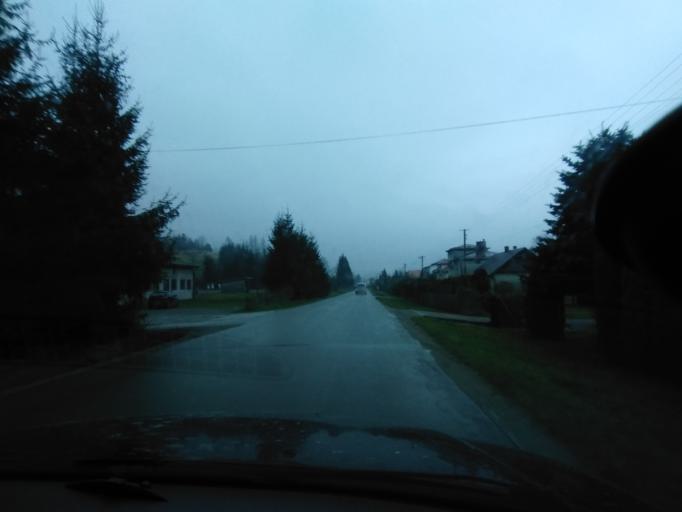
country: PL
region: Subcarpathian Voivodeship
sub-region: Powiat brzozowski
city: Wesola
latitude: 49.7512
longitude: 22.1181
